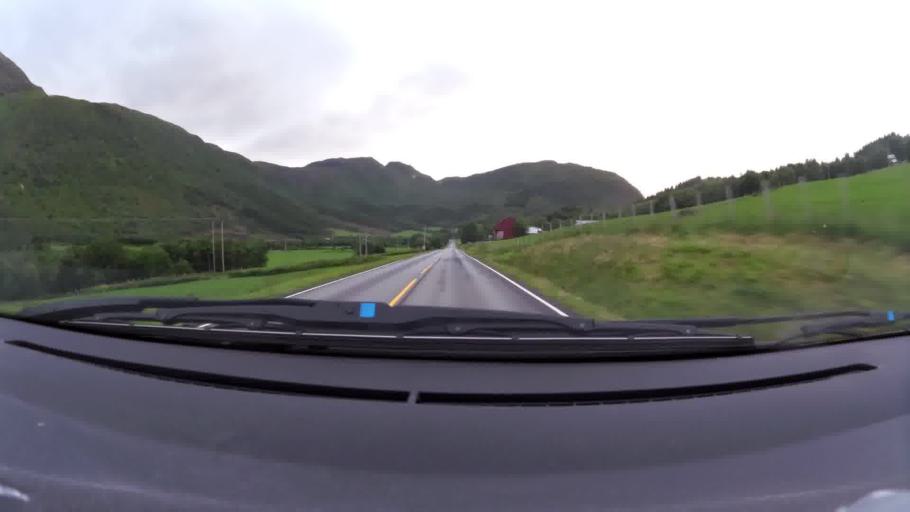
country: NO
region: More og Romsdal
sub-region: Molde
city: Molde
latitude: 62.7927
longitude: 7.2512
